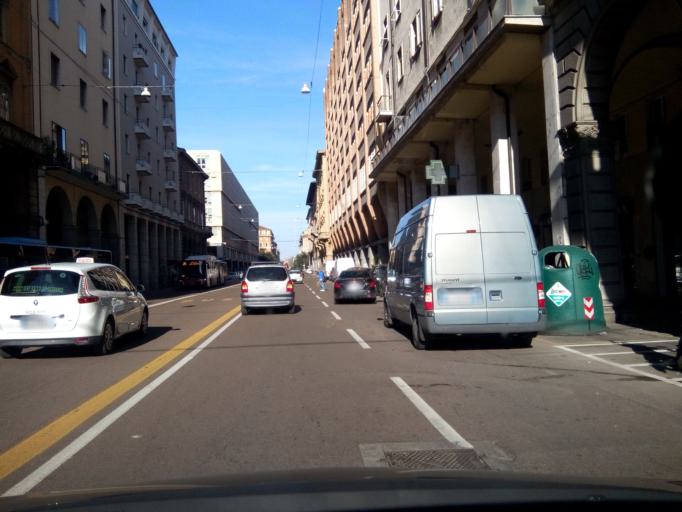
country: IT
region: Emilia-Romagna
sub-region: Provincia di Bologna
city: Bologna
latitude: 44.5014
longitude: 11.3435
